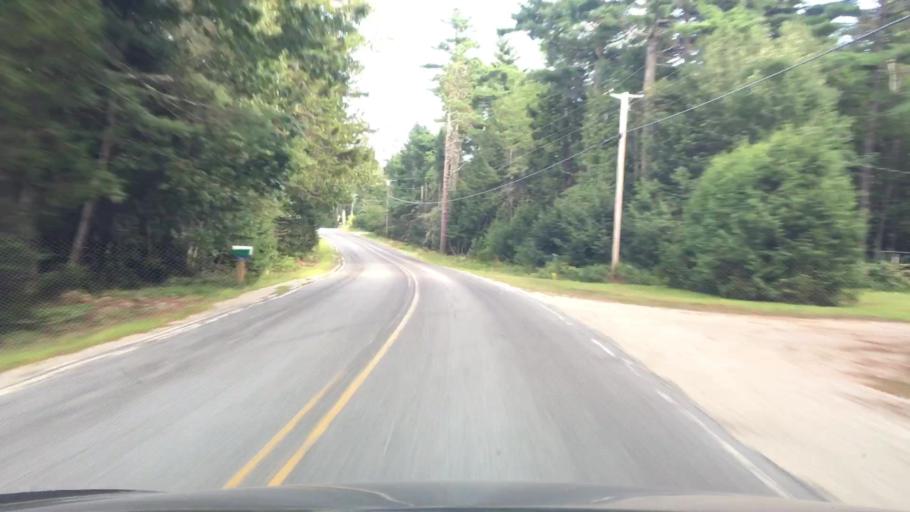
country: US
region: Maine
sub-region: Hancock County
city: Surry
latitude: 44.5075
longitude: -68.5960
